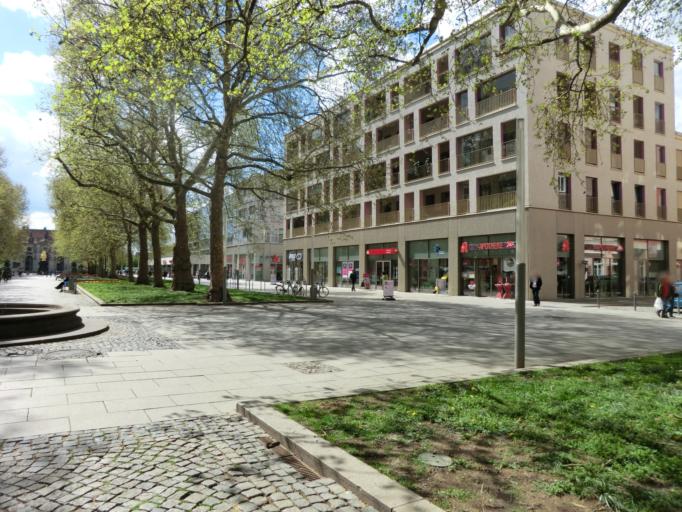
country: DE
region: Saxony
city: Dresden
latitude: 51.0596
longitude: 13.7429
